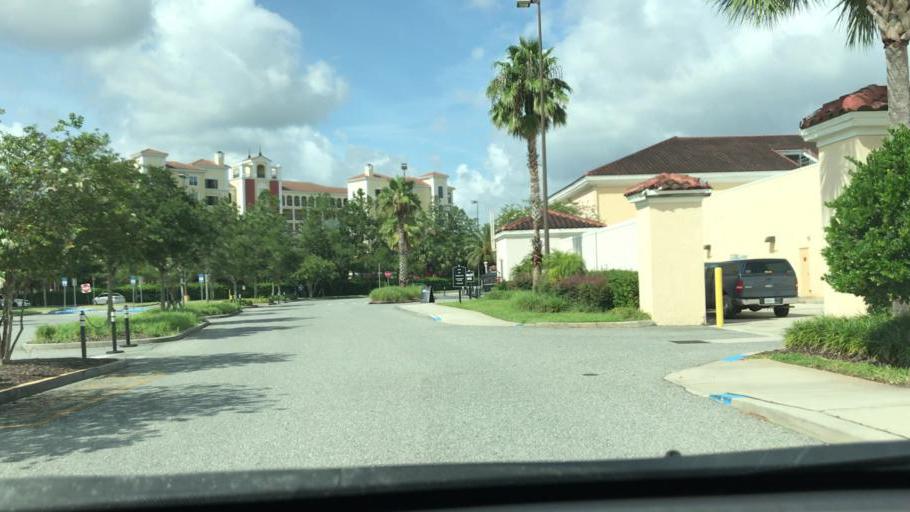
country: US
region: Florida
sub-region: Orange County
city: Williamsburg
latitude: 28.3869
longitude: -81.4907
